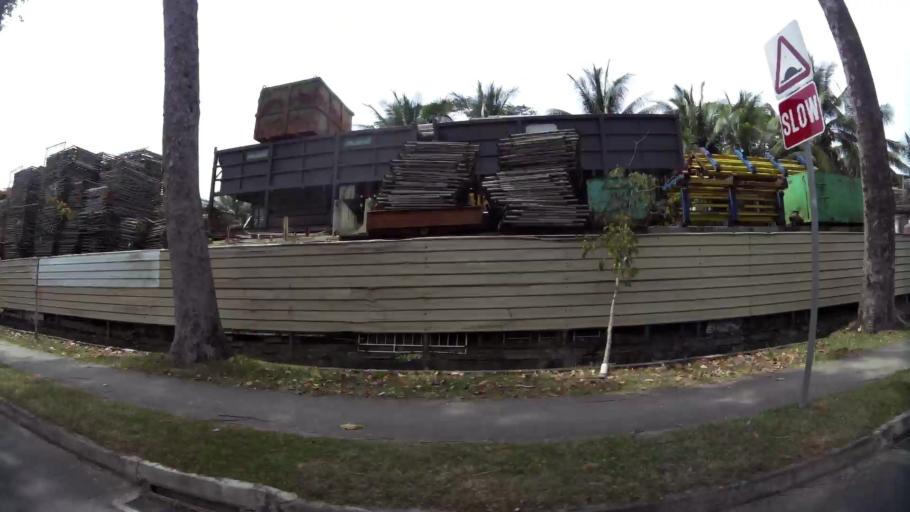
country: MY
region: Johor
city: Johor Bahru
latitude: 1.4053
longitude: 103.7550
